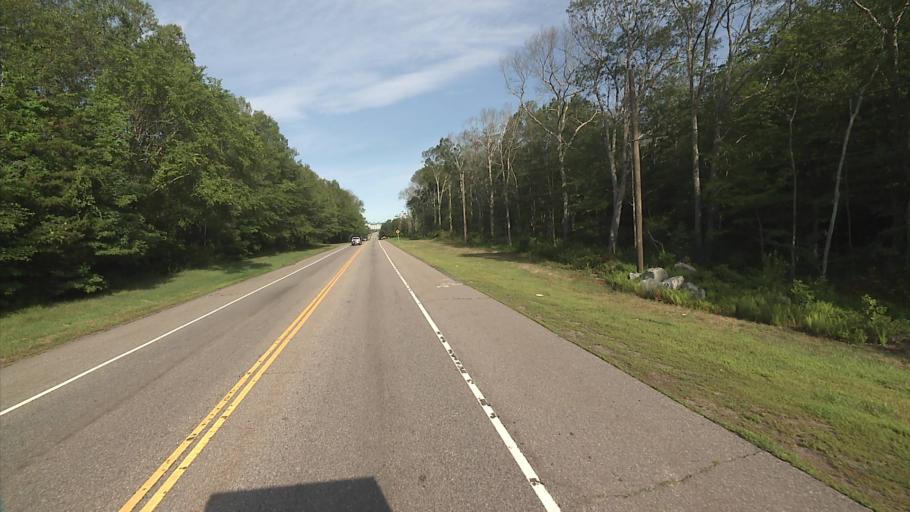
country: US
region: Connecticut
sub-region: New London County
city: Preston City
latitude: 41.4664
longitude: -71.9356
